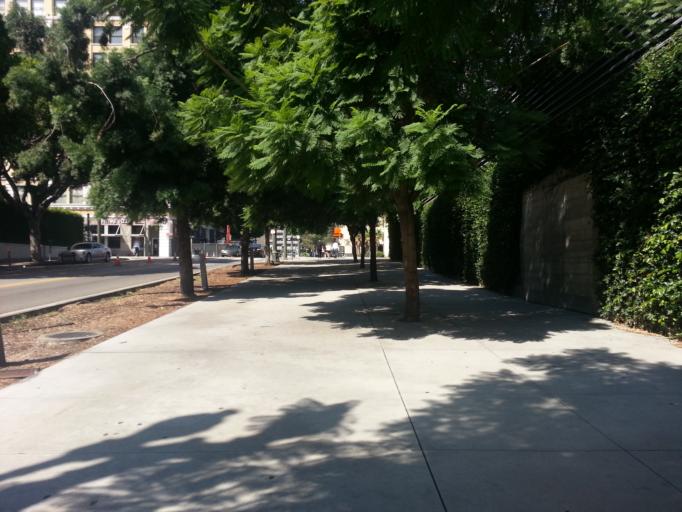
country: US
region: California
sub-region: Los Angeles County
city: Los Angeles
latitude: 34.0507
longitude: -118.2439
